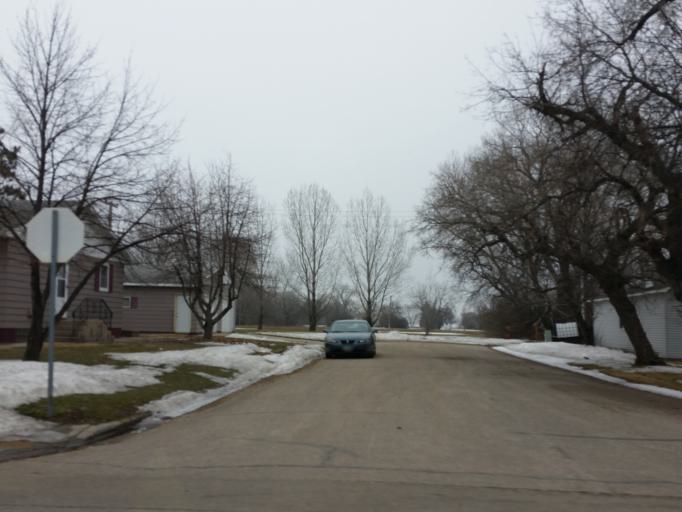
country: US
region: North Dakota
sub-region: Walsh County
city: Grafton
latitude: 48.6201
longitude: -97.4489
